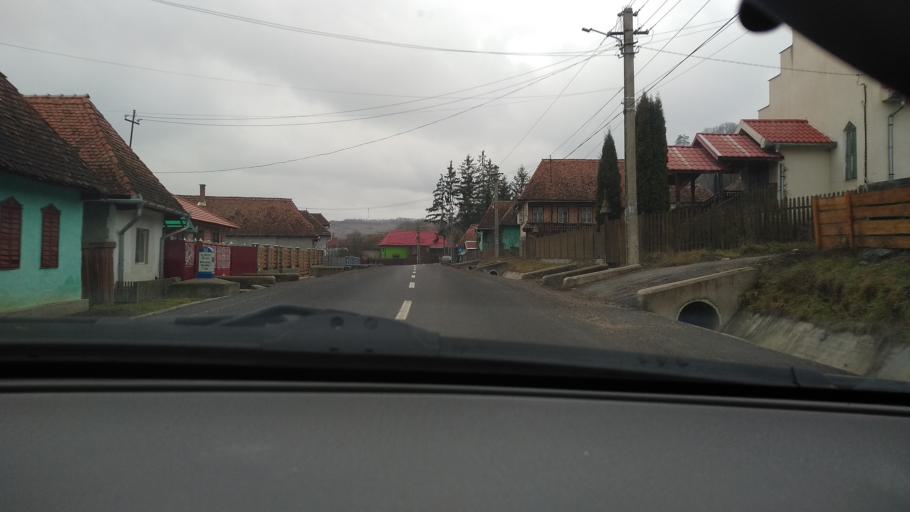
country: RO
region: Mures
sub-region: Comuna Magherani
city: Magherani
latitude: 46.5637
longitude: 24.9122
